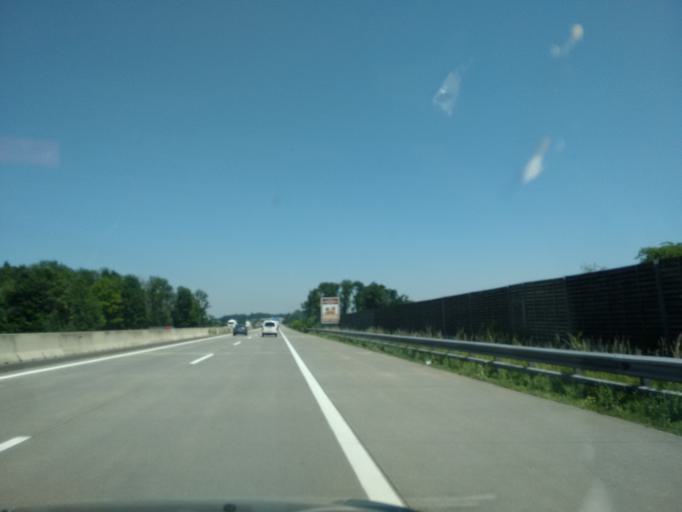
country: AT
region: Upper Austria
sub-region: Wels-Land
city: Sattledt
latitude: 48.0492
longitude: 14.0139
